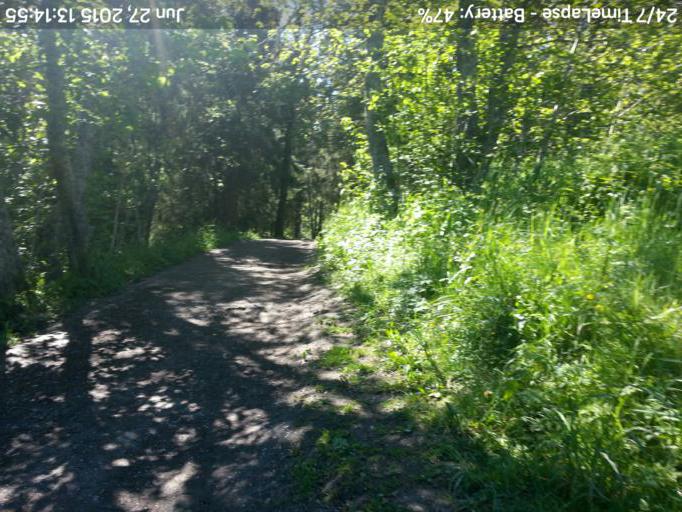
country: NO
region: Sor-Trondelag
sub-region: Trondheim
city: Trondheim
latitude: 63.4014
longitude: 10.3133
